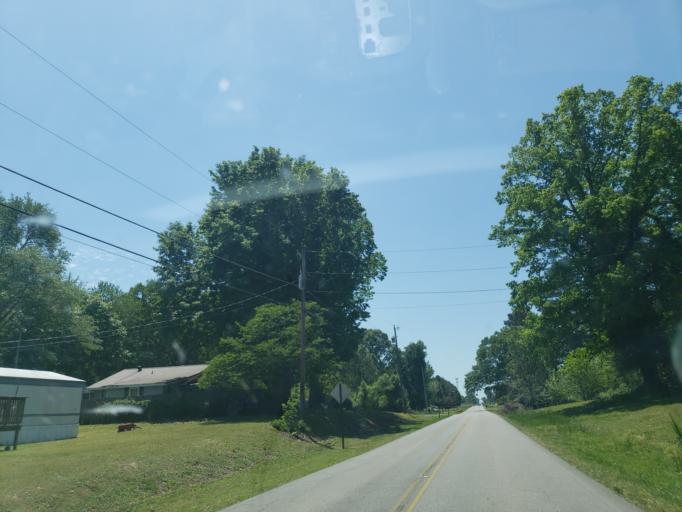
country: US
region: Alabama
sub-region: Madison County
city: Harvest
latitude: 34.8969
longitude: -86.7339
